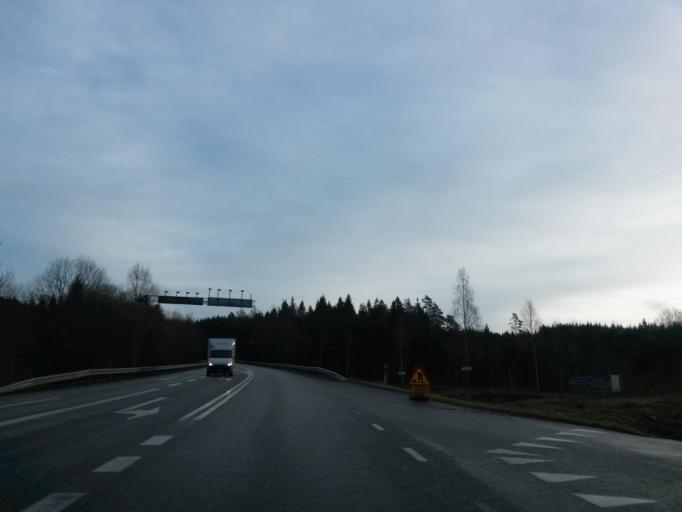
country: SE
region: Vaestra Goetaland
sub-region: Marks Kommun
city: Bua
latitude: 57.5088
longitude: 12.5832
